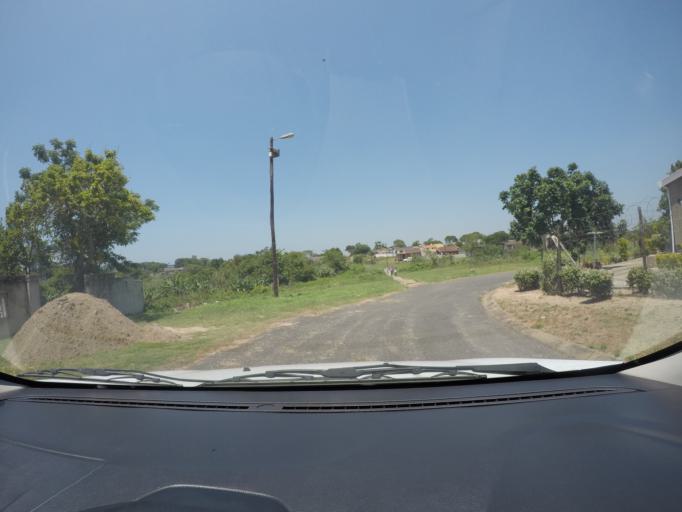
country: ZA
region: KwaZulu-Natal
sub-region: uThungulu District Municipality
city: eSikhawini
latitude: -28.8746
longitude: 31.9138
